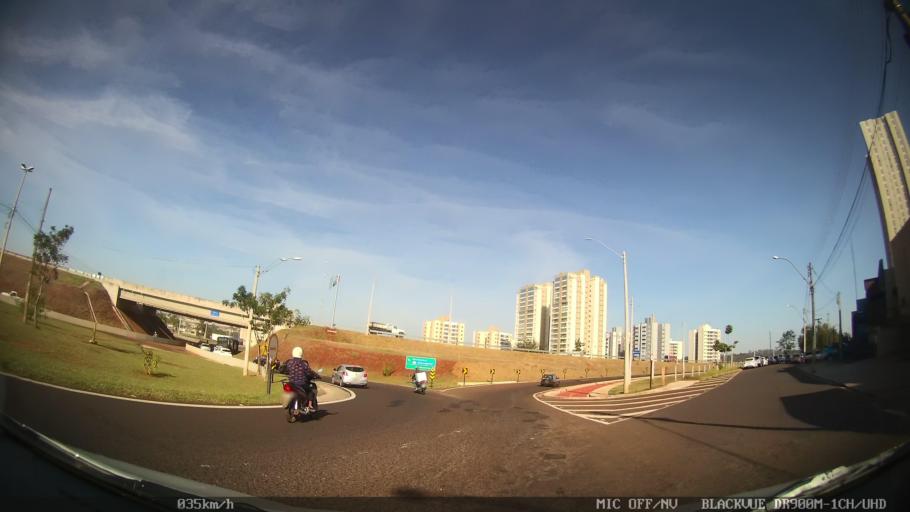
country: BR
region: Sao Paulo
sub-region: Ribeirao Preto
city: Ribeirao Preto
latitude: -21.2189
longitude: -47.8272
